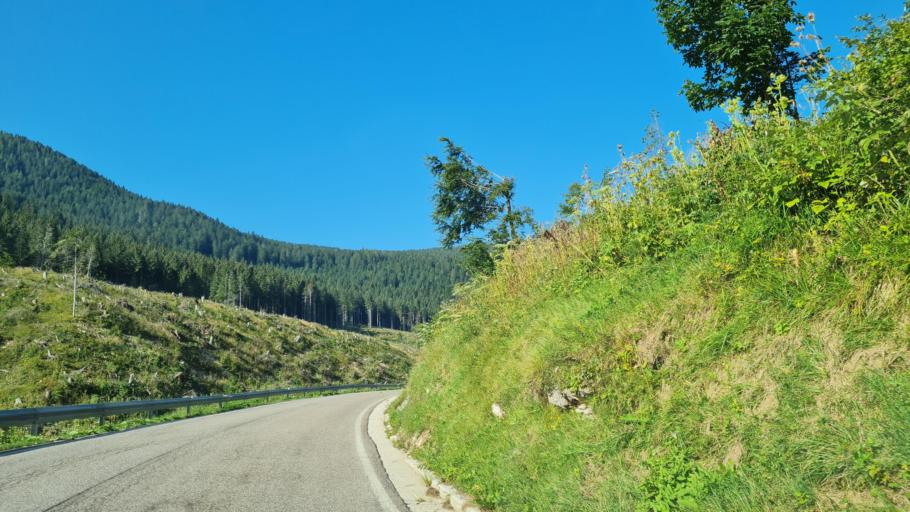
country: IT
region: Veneto
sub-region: Provincia di Vicenza
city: San Pietro Valdastico
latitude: 45.9463
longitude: 11.4088
